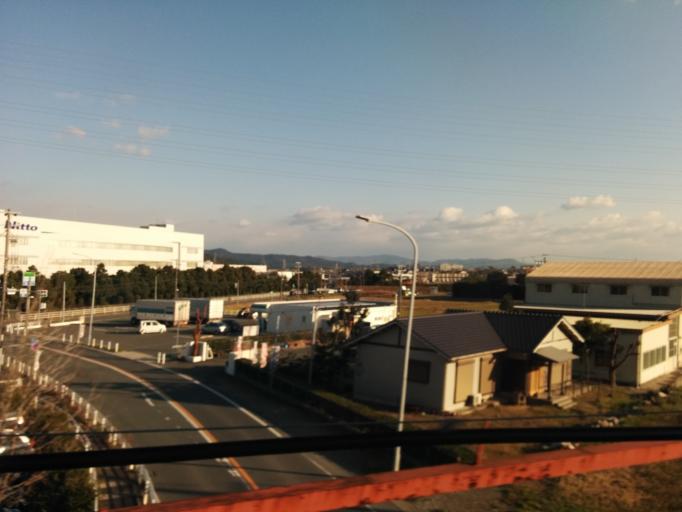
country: JP
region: Shizuoka
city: Kosai-shi
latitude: 34.7147
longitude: 137.4851
